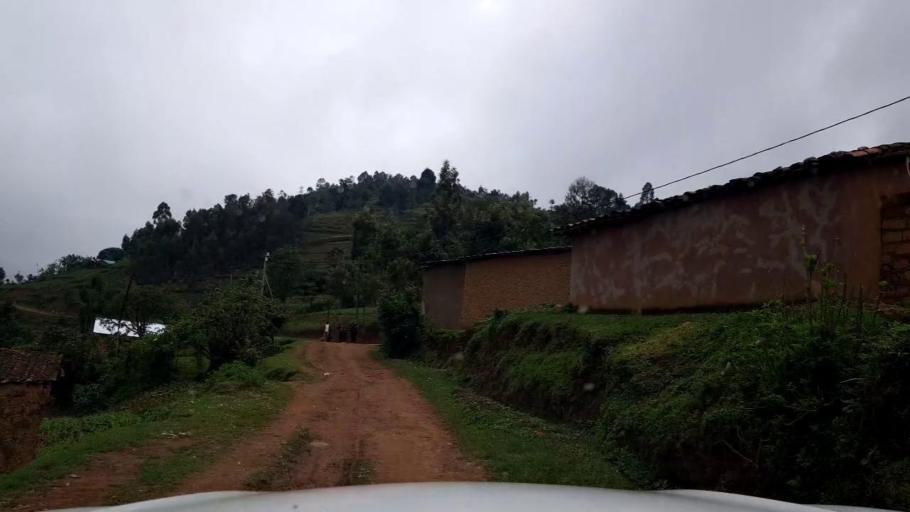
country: RW
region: Northern Province
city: Musanze
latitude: -1.5924
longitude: 29.7855
